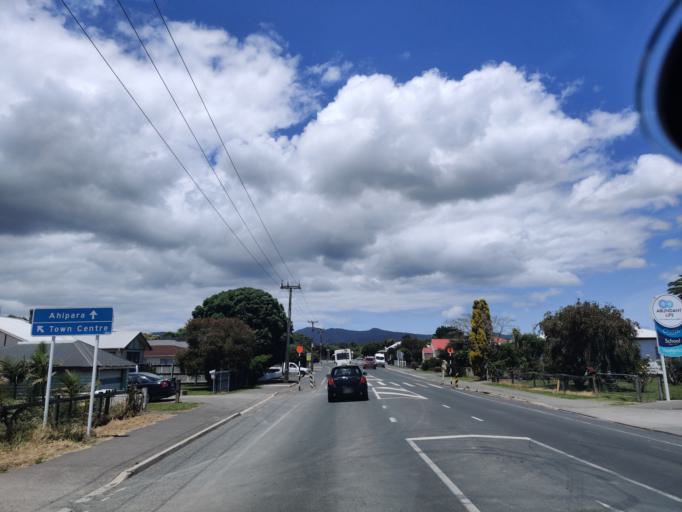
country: NZ
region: Northland
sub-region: Far North District
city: Kaitaia
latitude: -35.1074
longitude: 173.2587
